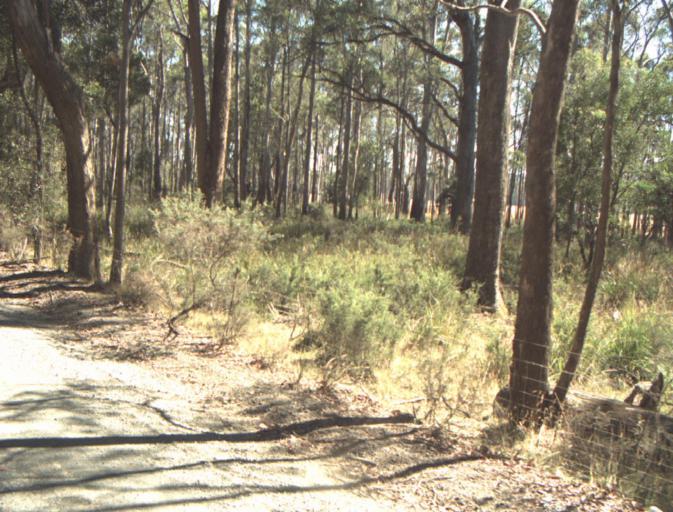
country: AU
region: Tasmania
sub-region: Launceston
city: Newstead
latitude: -41.3582
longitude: 147.2260
